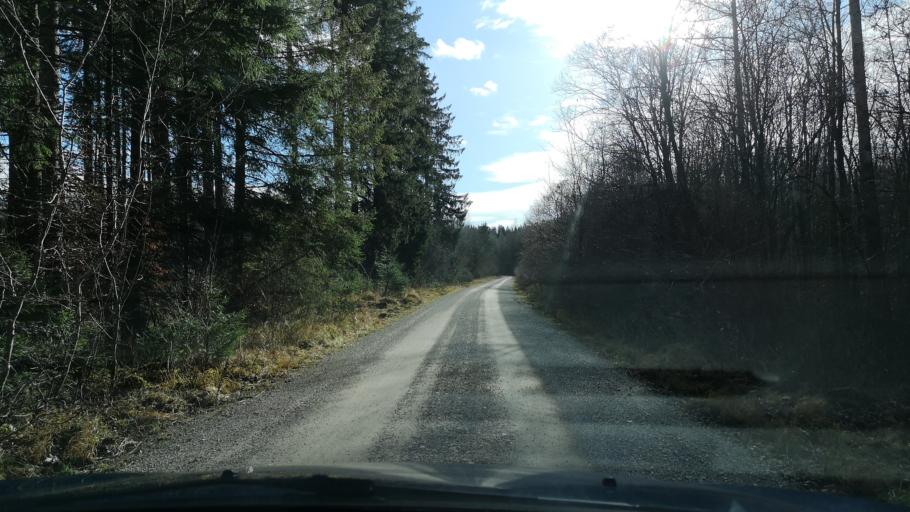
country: DE
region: Bavaria
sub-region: Upper Bavaria
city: Forstinning
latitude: 48.1196
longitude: 11.9086
